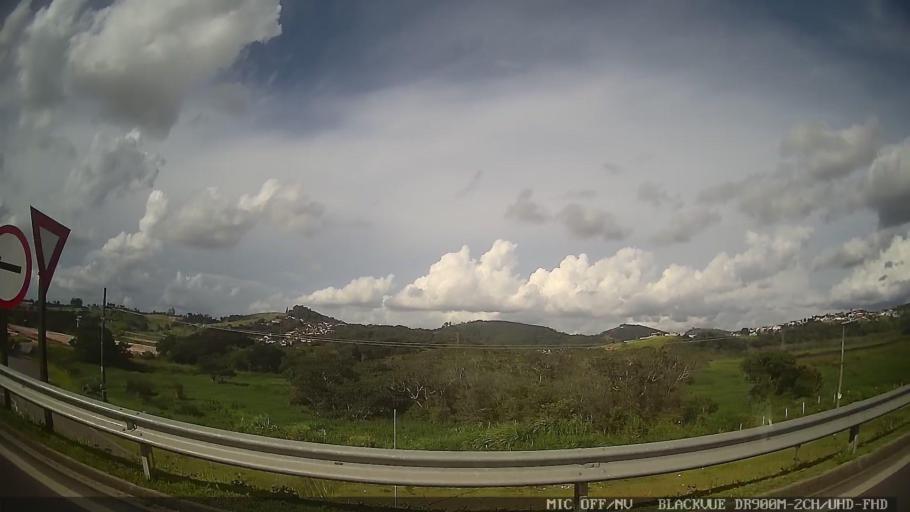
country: BR
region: Sao Paulo
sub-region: Bom Jesus Dos Perdoes
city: Bom Jesus dos Perdoes
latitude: -23.1334
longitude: -46.4638
